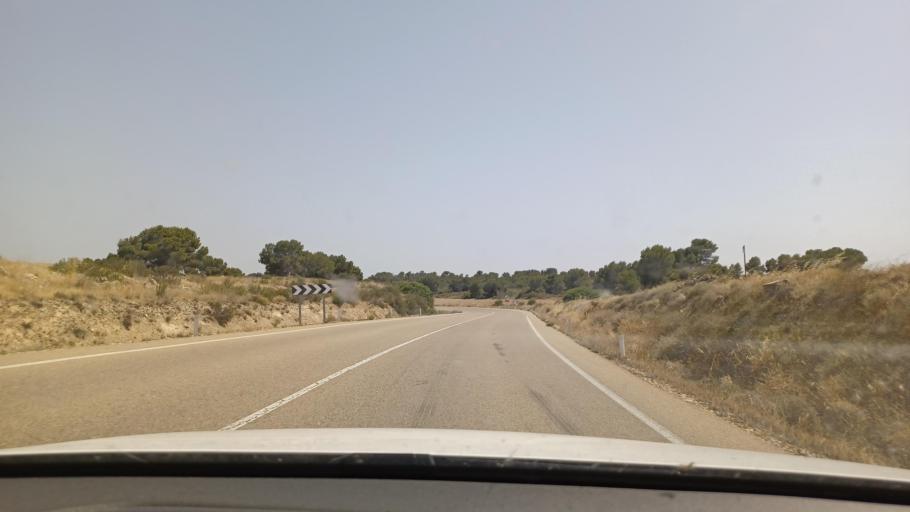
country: ES
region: Aragon
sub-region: Provincia de Zaragoza
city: Chiprana
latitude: 41.3650
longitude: -0.1073
